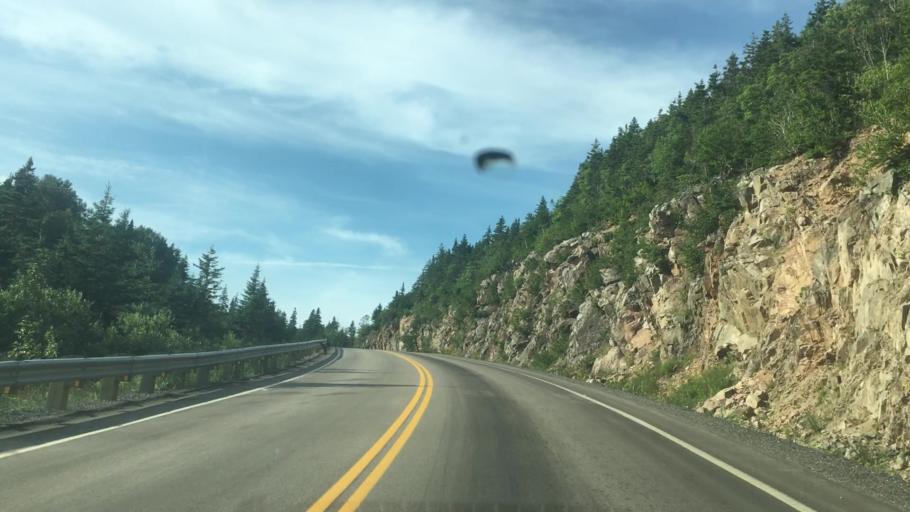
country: CA
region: Nova Scotia
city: Sydney Mines
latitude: 46.8220
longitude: -60.6545
